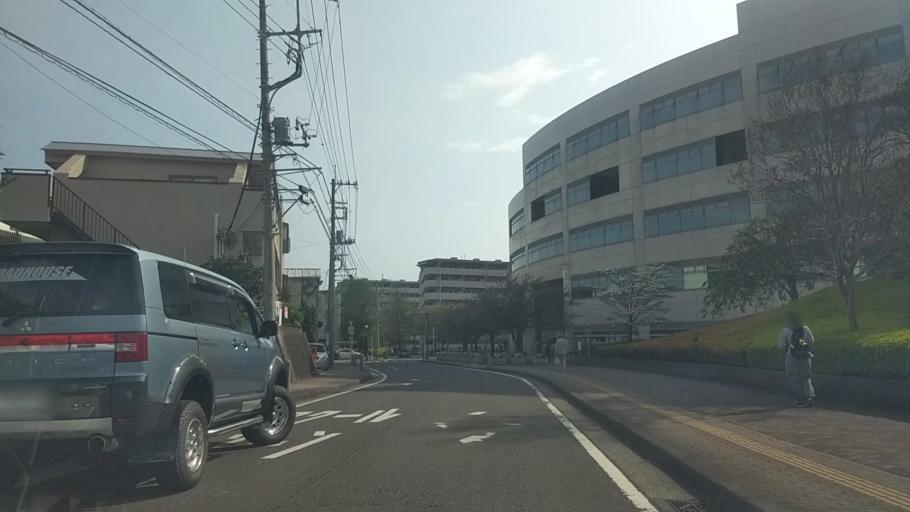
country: JP
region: Kanagawa
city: Kamakura
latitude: 35.3686
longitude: 139.5542
